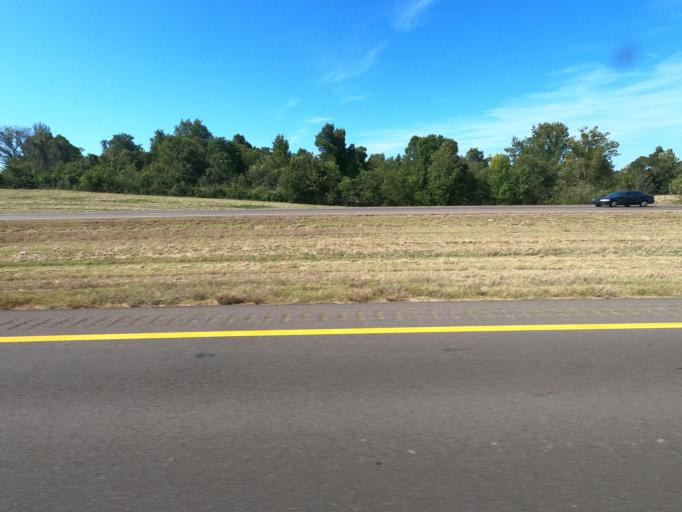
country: US
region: Tennessee
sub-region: Obion County
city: Obion
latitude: 36.2934
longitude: -89.1989
